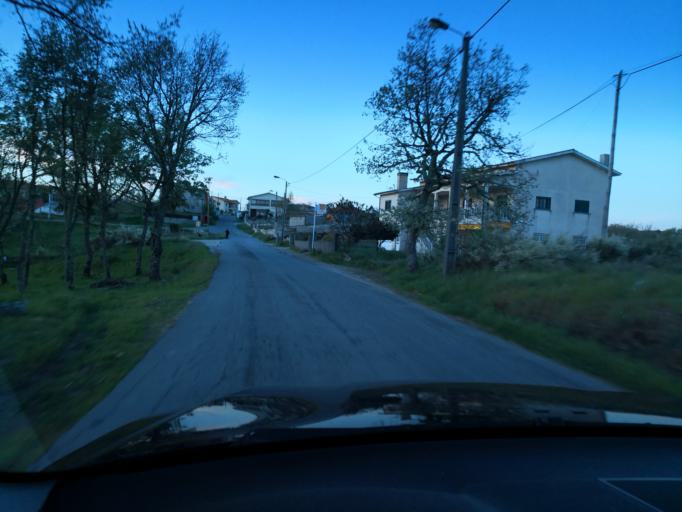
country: PT
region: Vila Real
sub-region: Vila Real
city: Vila Real
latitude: 41.3544
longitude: -7.6631
